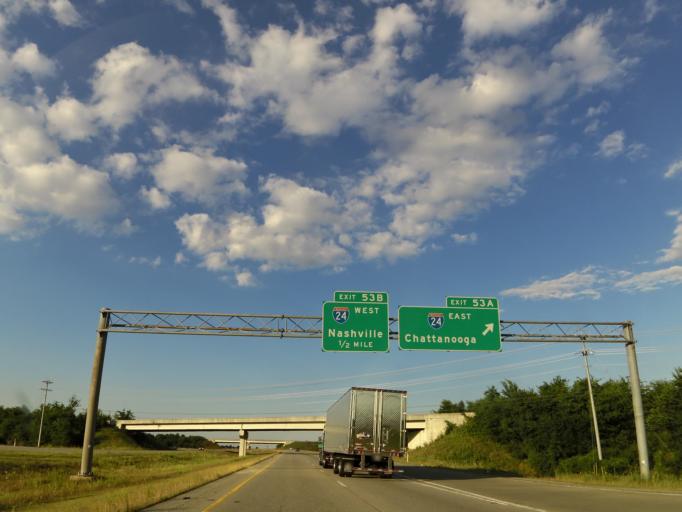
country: US
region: Tennessee
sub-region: Rutherford County
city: Murfreesboro
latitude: 35.8800
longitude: -86.4827
